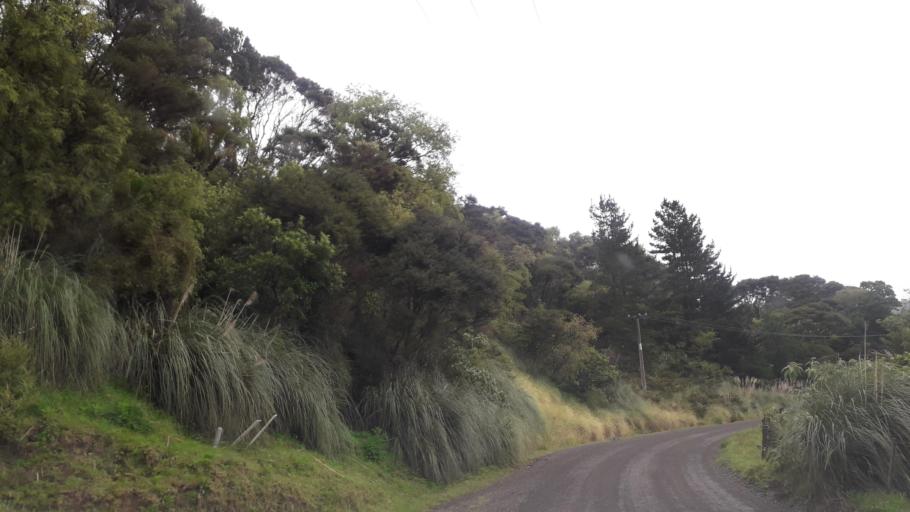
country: NZ
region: Northland
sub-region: Far North District
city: Ahipara
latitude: -35.4400
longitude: 173.3103
